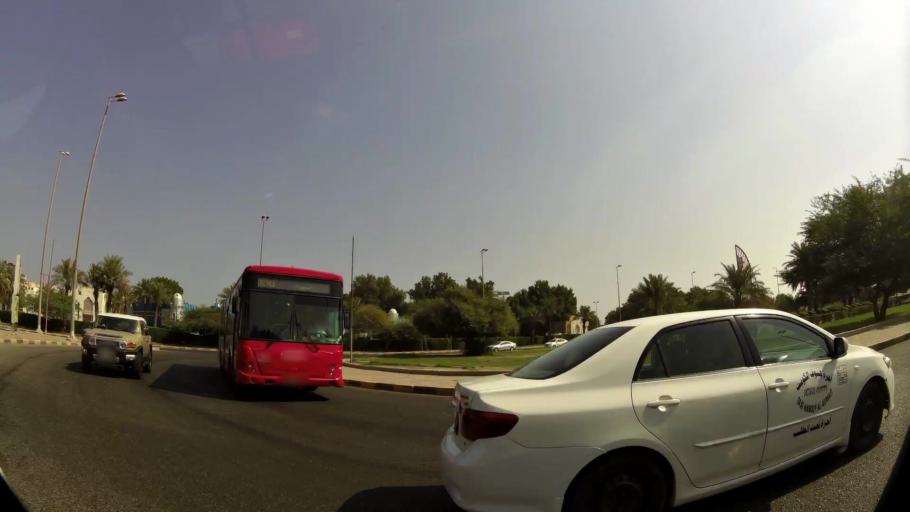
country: KW
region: Al Ahmadi
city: Al Mahbulah
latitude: 29.1324
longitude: 48.1310
